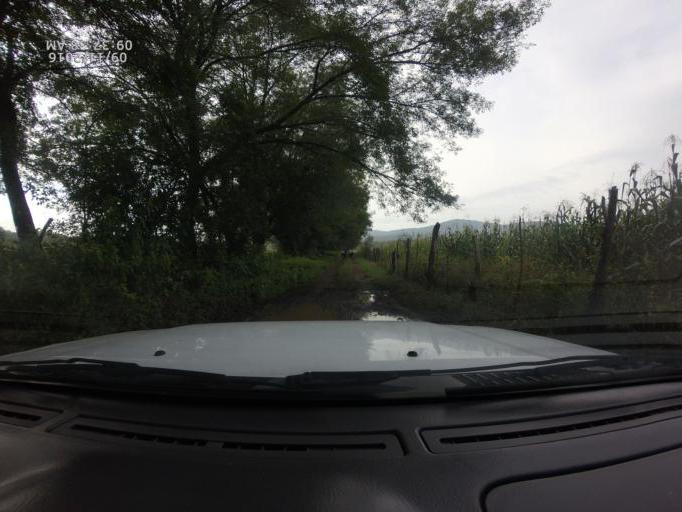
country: MX
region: Michoacan
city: Acuitzio del Canje
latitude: 19.5678
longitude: -101.2895
